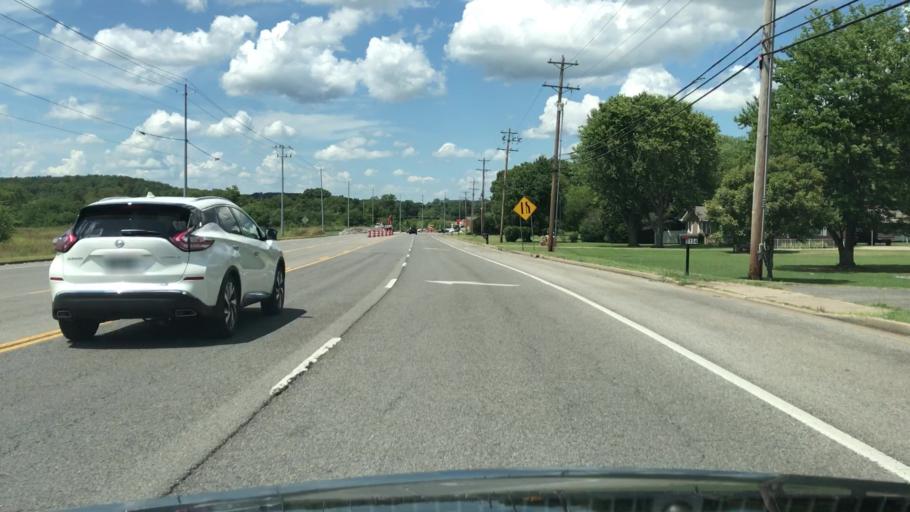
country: US
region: Tennessee
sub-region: Rutherford County
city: Murfreesboro
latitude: 35.8443
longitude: -86.4850
